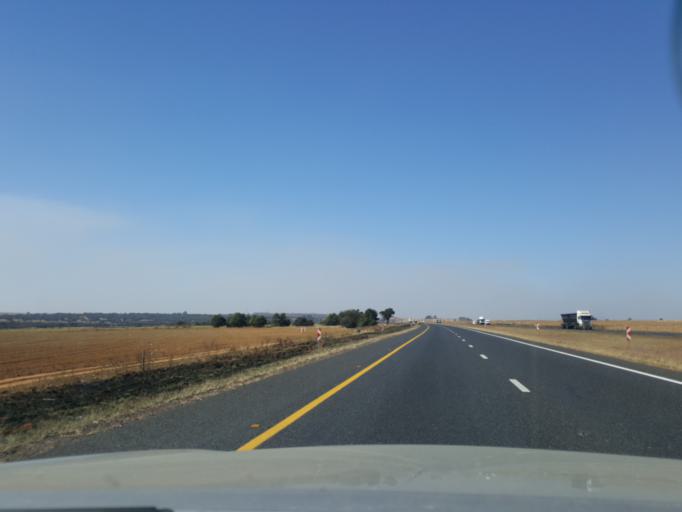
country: ZA
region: Mpumalanga
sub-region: Nkangala District Municipality
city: Delmas
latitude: -26.0190
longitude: 28.9190
